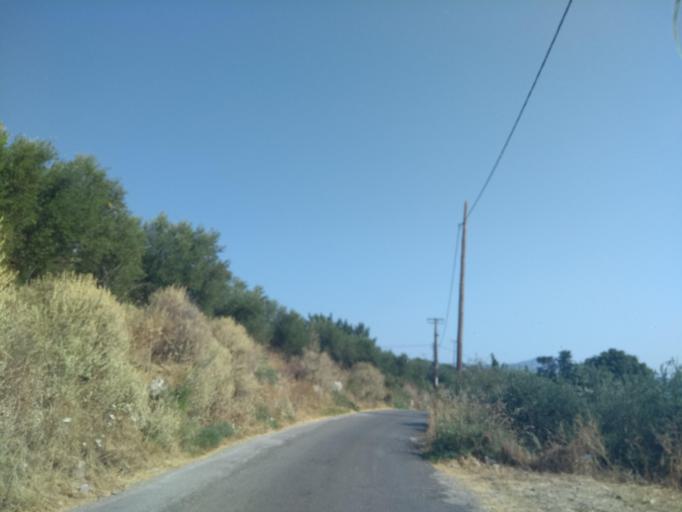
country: GR
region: Crete
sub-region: Nomos Chanias
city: Kalivai
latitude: 35.4324
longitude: 24.1757
